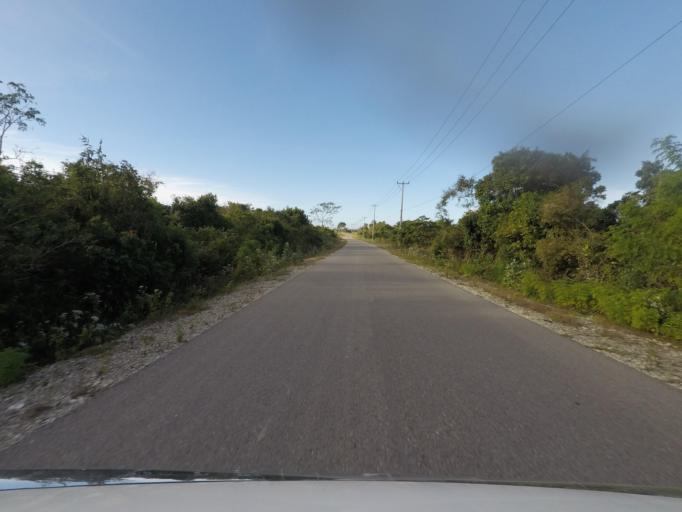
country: TL
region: Lautem
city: Lospalos
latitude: -8.3981
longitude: 127.0066
